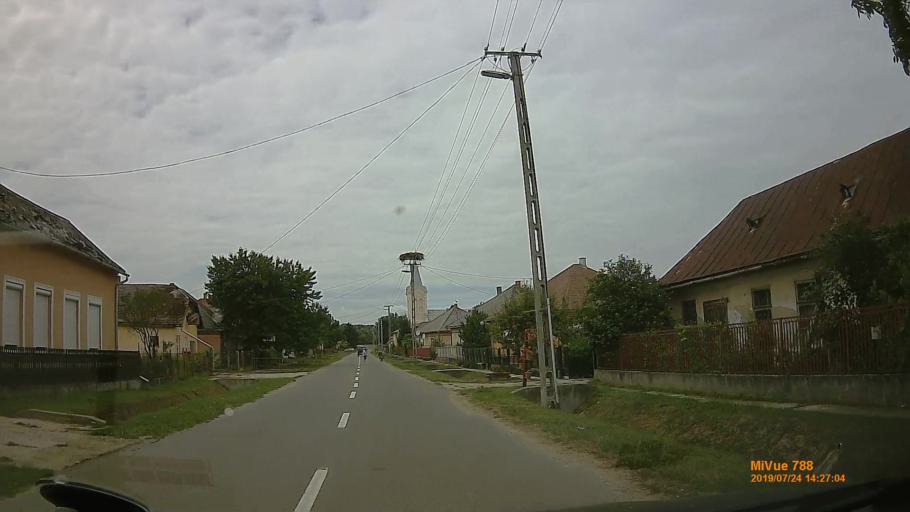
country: HU
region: Szabolcs-Szatmar-Bereg
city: Mandok
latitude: 48.3307
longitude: 22.2653
